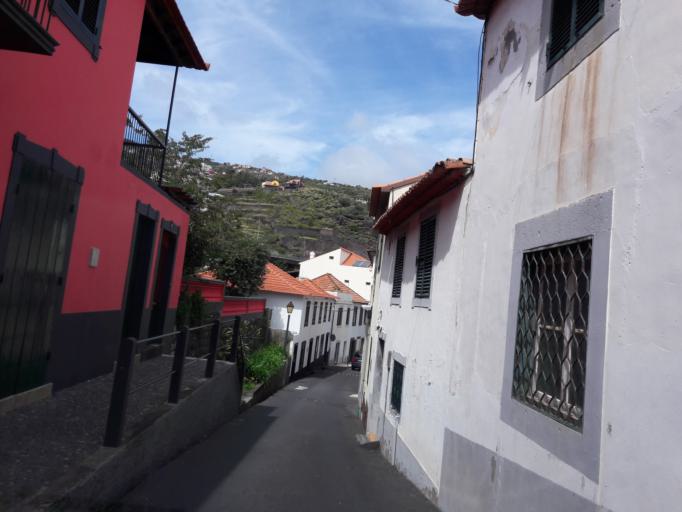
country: PT
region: Madeira
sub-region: Santa Cruz
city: Santa Cruz
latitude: 32.6864
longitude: -16.7933
